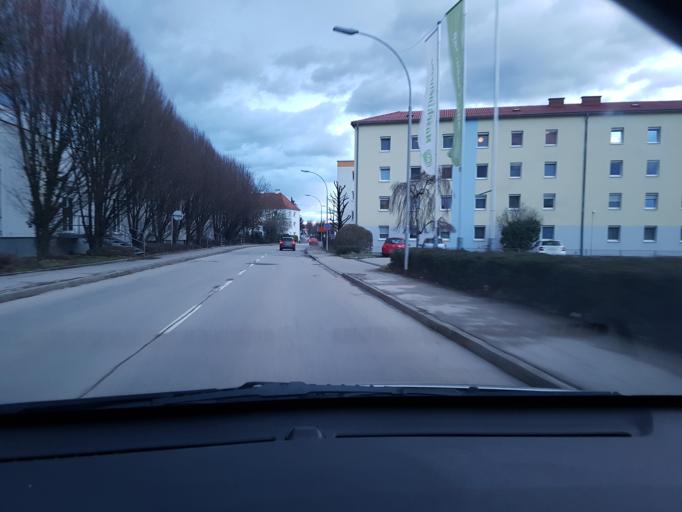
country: AT
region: Upper Austria
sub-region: Steyr Stadt
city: Steyr
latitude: 48.0475
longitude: 14.4153
